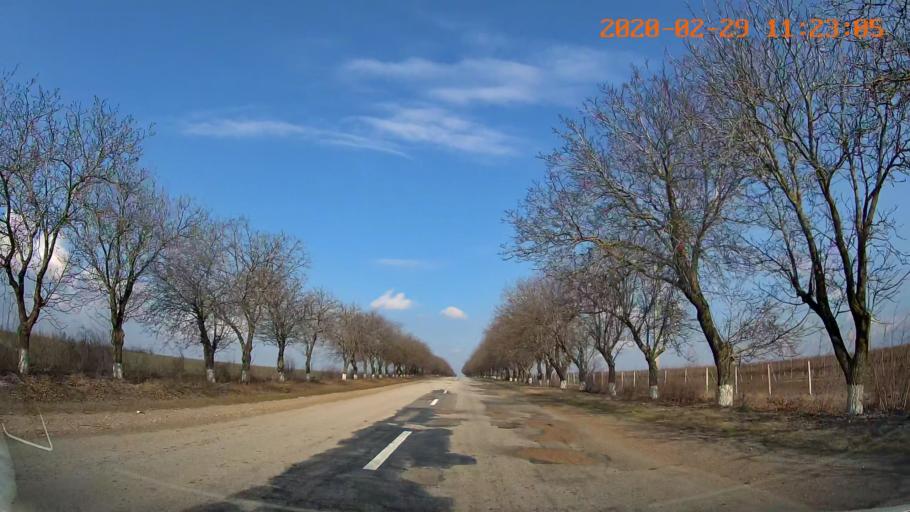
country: MD
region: Telenesti
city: Cocieri
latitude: 47.4030
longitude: 29.1603
